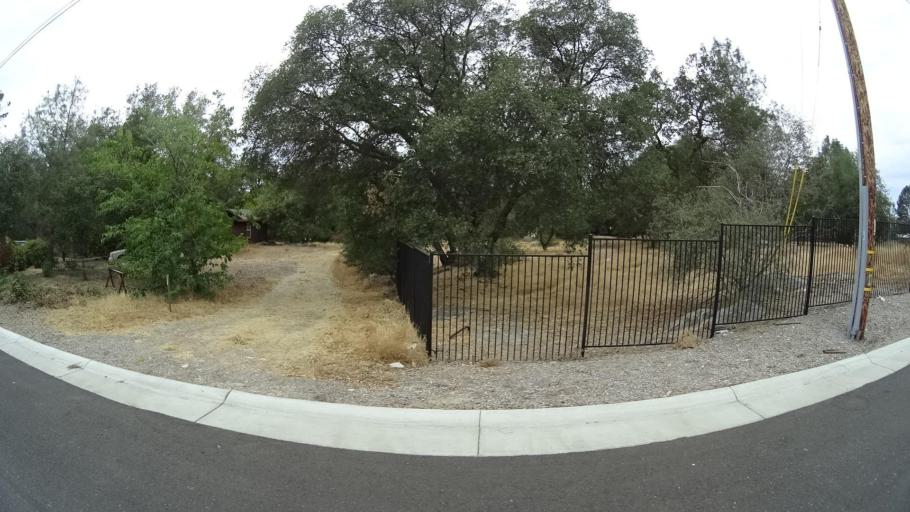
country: US
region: California
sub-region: Placer County
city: Rocklin
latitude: 38.7869
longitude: -121.2346
